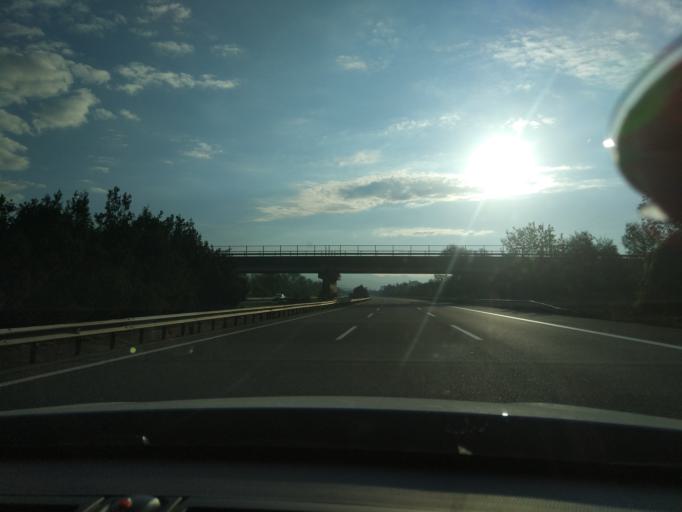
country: TR
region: Duzce
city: Duzce
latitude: 40.7914
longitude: 31.2140
